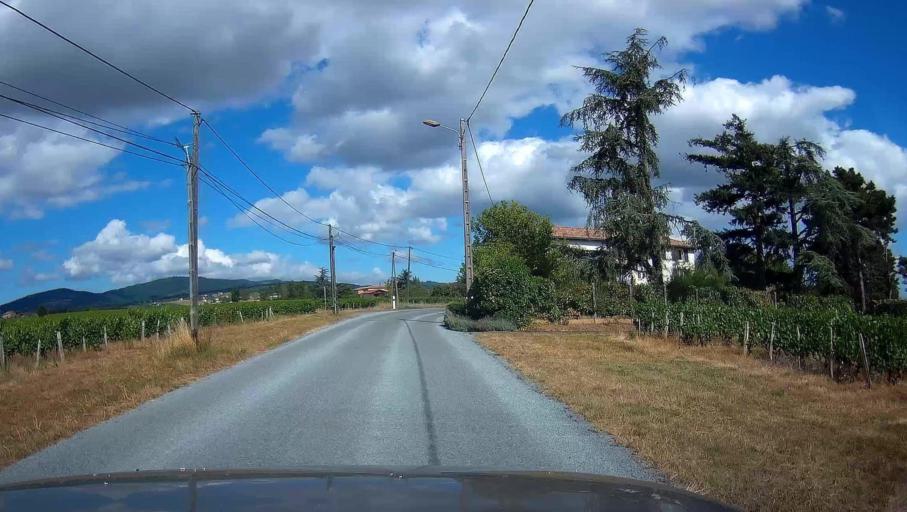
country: FR
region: Rhone-Alpes
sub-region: Departement du Rhone
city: Liergues
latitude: 45.9742
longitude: 4.6518
